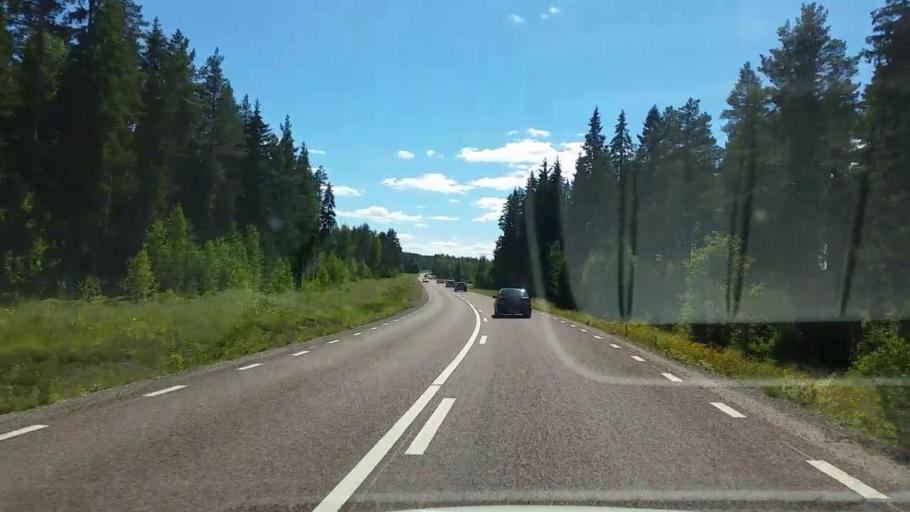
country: SE
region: Gaevleborg
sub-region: Ovanakers Kommun
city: Edsbyn
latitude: 61.2773
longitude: 15.8959
